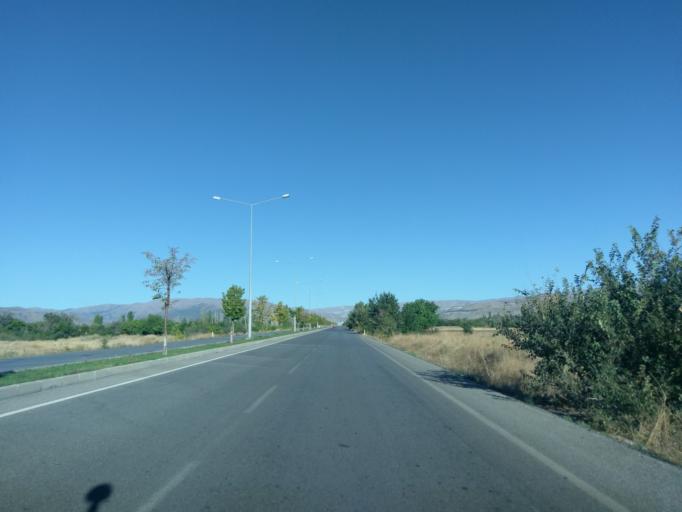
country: TR
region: Erzincan
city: Erzincan
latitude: 39.7785
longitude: 39.4126
